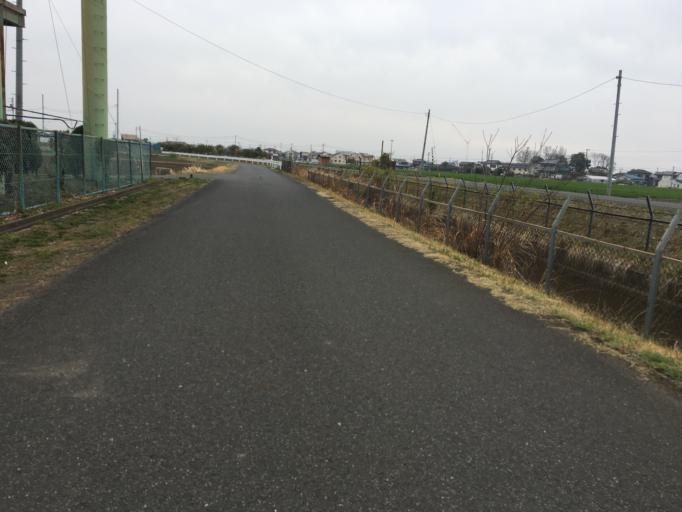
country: JP
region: Saitama
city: Kazo
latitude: 36.1083
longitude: 139.5950
